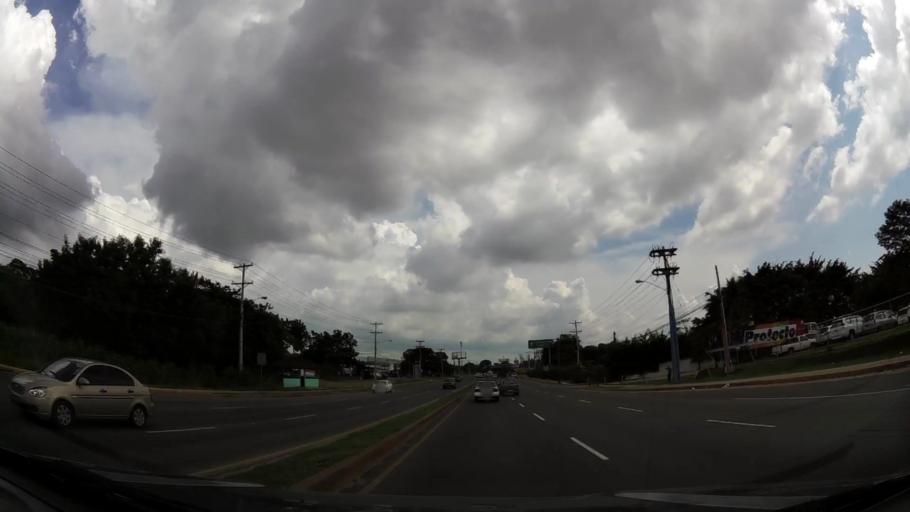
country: PA
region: Panama
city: Tocumen
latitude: 9.0675
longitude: -79.4107
